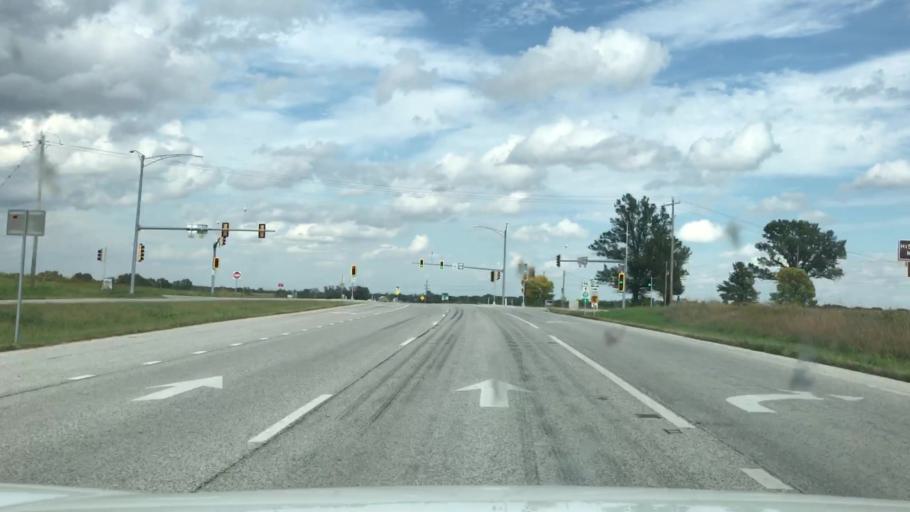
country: US
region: Illinois
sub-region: Adams County
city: Quincy
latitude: 40.0075
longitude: -91.3686
